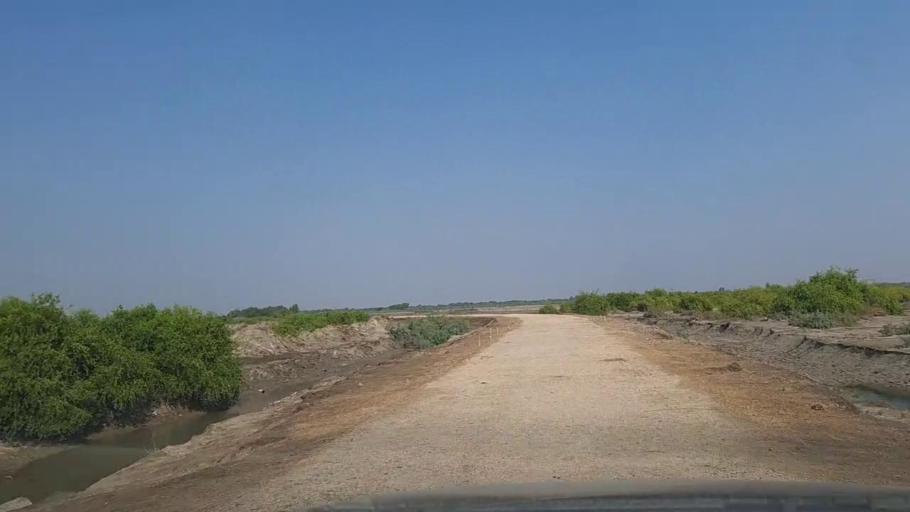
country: PK
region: Sindh
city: Mirpur Sakro
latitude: 24.5059
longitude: 67.7809
